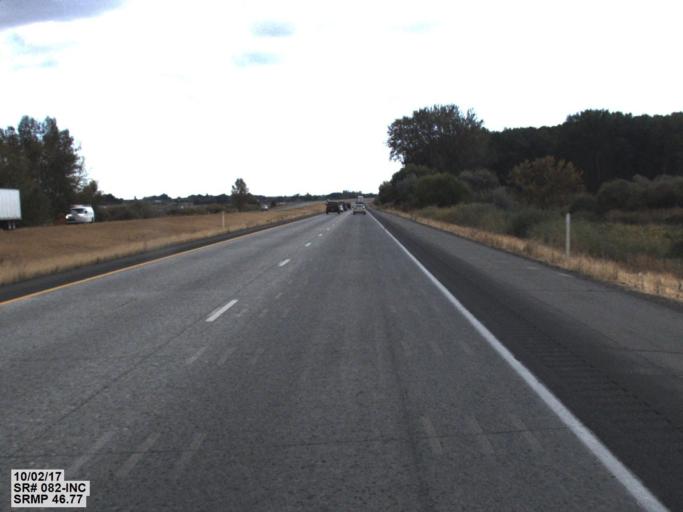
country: US
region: Washington
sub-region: Yakima County
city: Wapato
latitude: 46.4490
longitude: -120.3567
